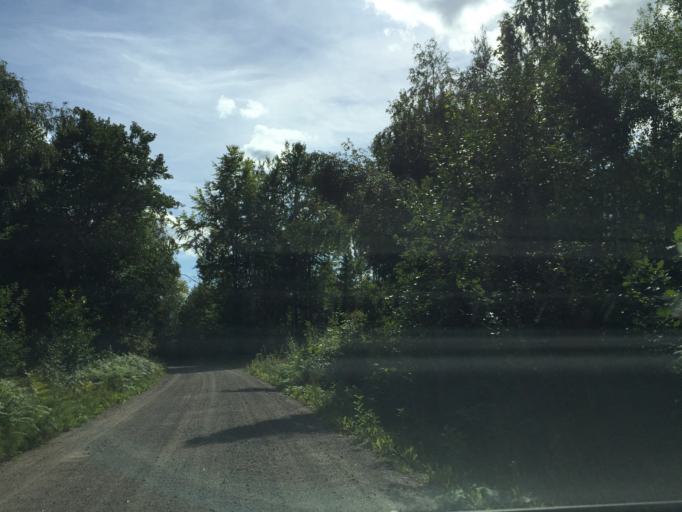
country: NO
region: Vestfold
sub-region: Holmestrand
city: Gullhaug
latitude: 59.4422
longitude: 10.1587
